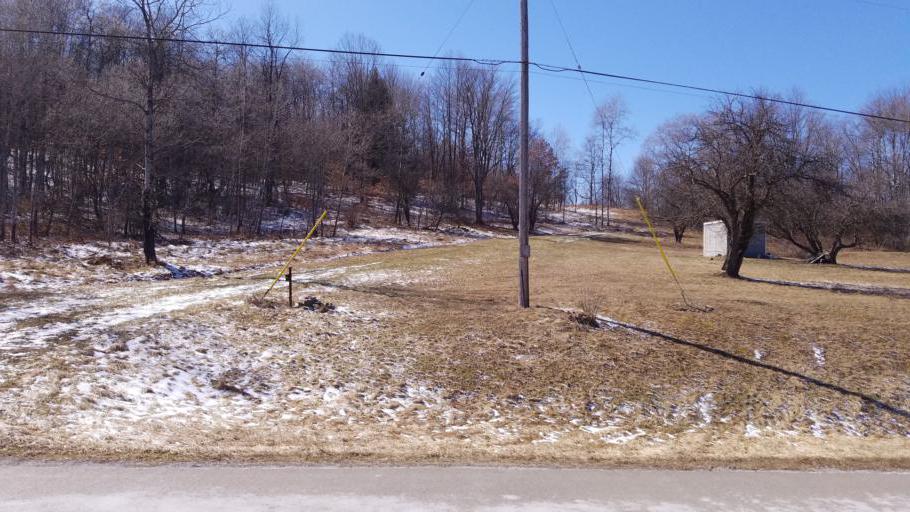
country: US
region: New York
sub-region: Allegany County
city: Wellsville
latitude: 42.0035
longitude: -77.8857
